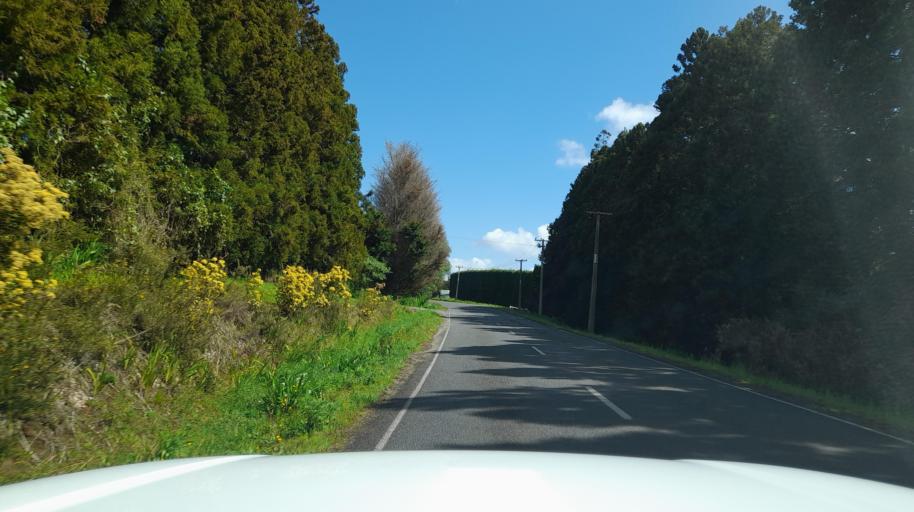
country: NZ
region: Northland
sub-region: Far North District
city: Kerikeri
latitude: -35.2360
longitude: 173.9006
